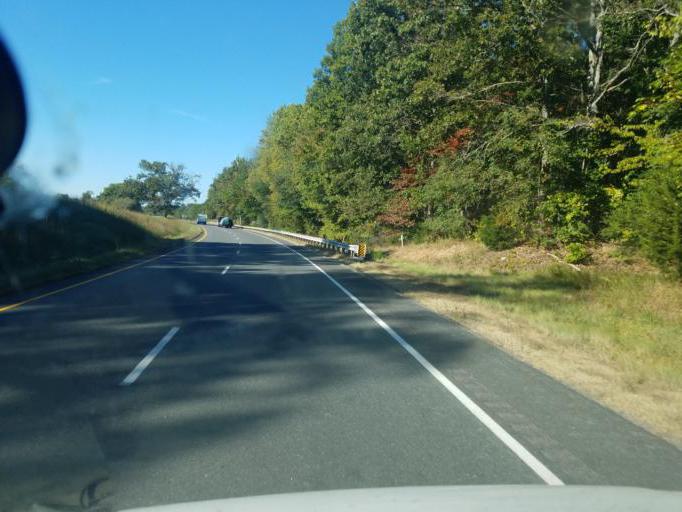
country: US
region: Virginia
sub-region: Madison County
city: Brightwood
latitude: 38.4175
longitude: -78.2036
